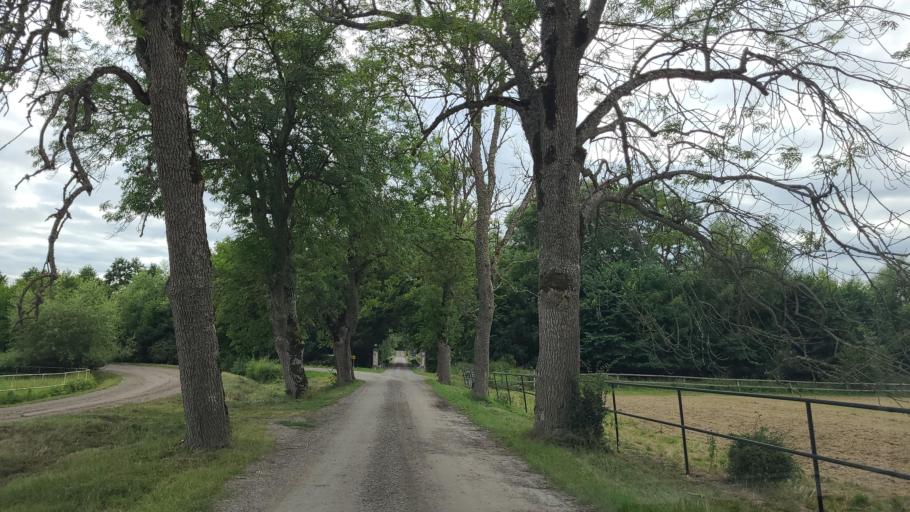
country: SE
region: Stockholm
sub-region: Upplands-Bro Kommun
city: Bro
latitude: 59.4662
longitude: 17.5883
